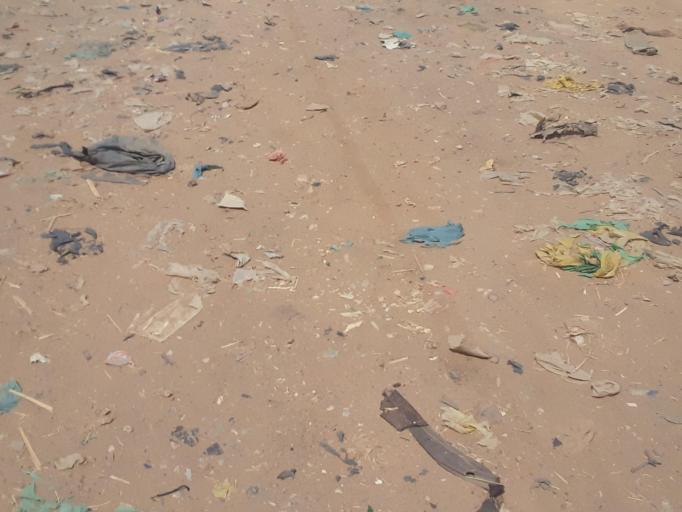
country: ZM
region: Lusaka
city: Lusaka
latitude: -15.3677
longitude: 28.2900
